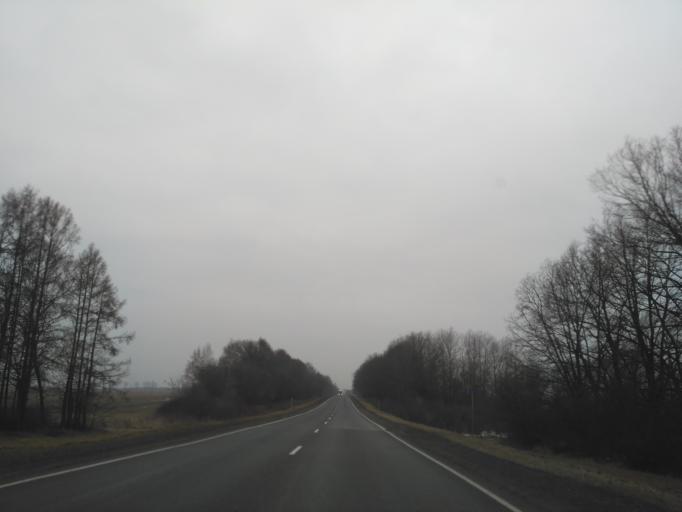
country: BY
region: Brest
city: Baranovichi
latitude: 53.2205
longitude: 26.1637
